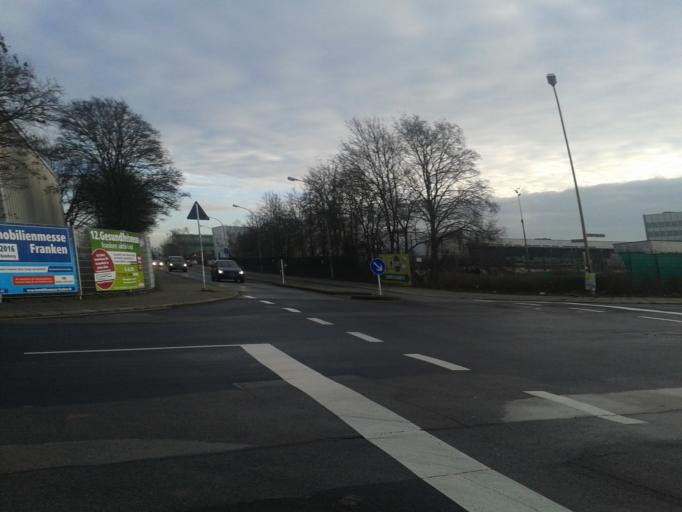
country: DE
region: Bavaria
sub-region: Upper Franconia
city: Hallstadt
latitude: 49.9126
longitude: 10.8761
